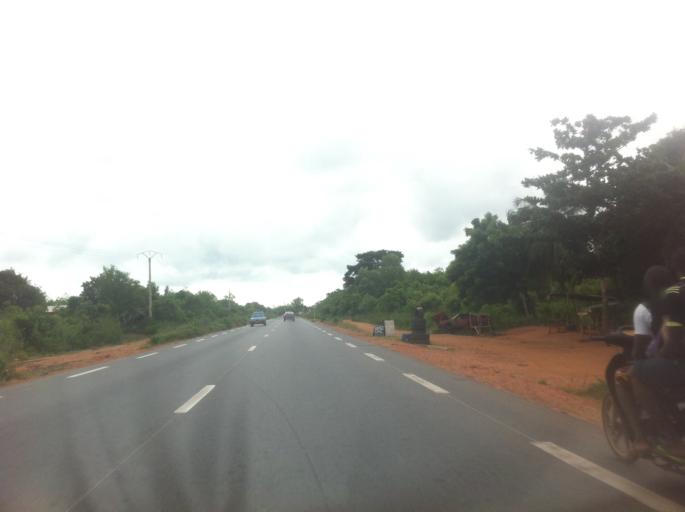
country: BJ
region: Atlantique
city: Ouidah
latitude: 6.3680
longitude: 2.0411
